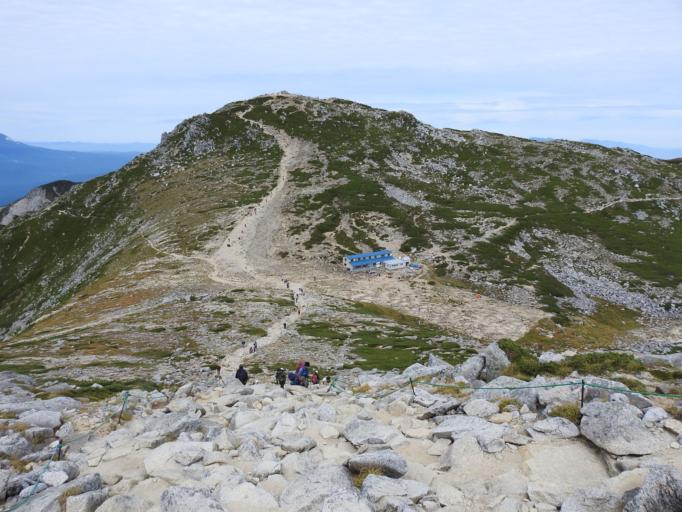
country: JP
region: Nagano
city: Ina
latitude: 35.7862
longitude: 137.8076
